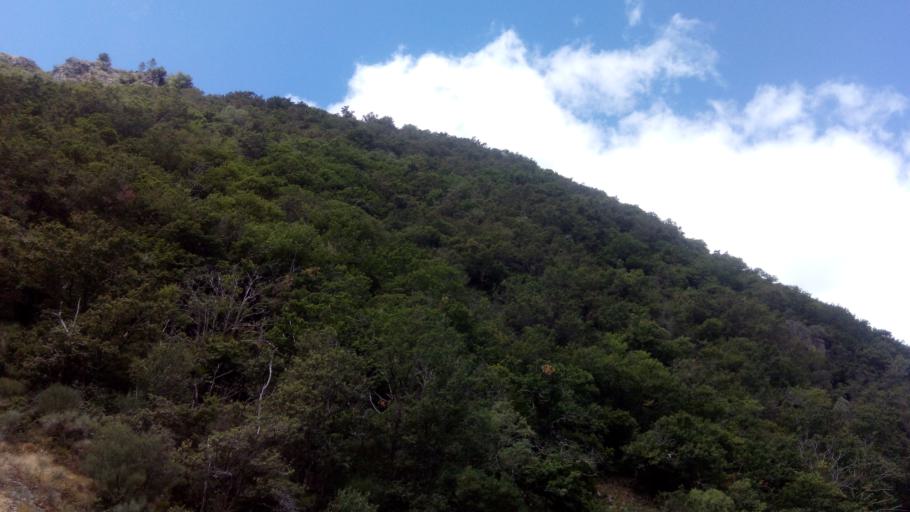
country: ES
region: Galicia
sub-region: Provincia de Lugo
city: Sober
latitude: 42.4007
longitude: -7.6293
